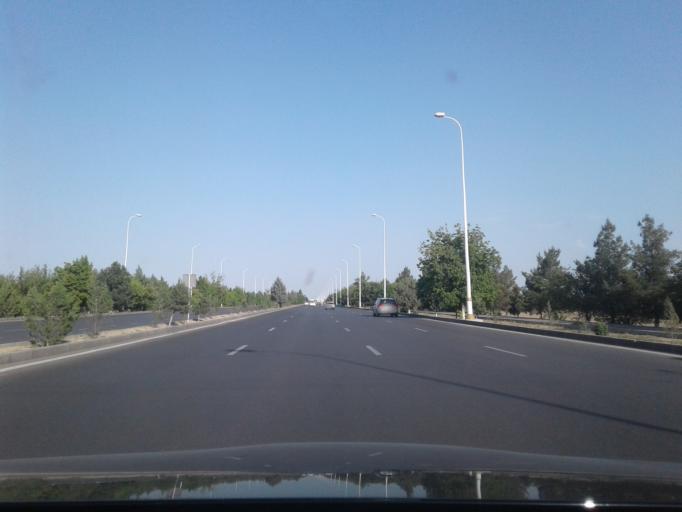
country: TM
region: Ahal
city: Abadan
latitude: 38.0052
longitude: 58.2896
